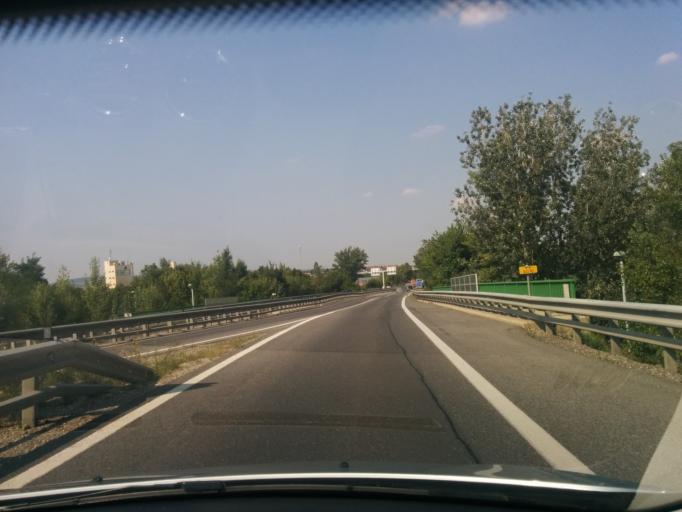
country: AT
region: Lower Austria
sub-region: Politischer Bezirk Korneuburg
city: Bisamberg
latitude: 48.3322
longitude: 16.3374
